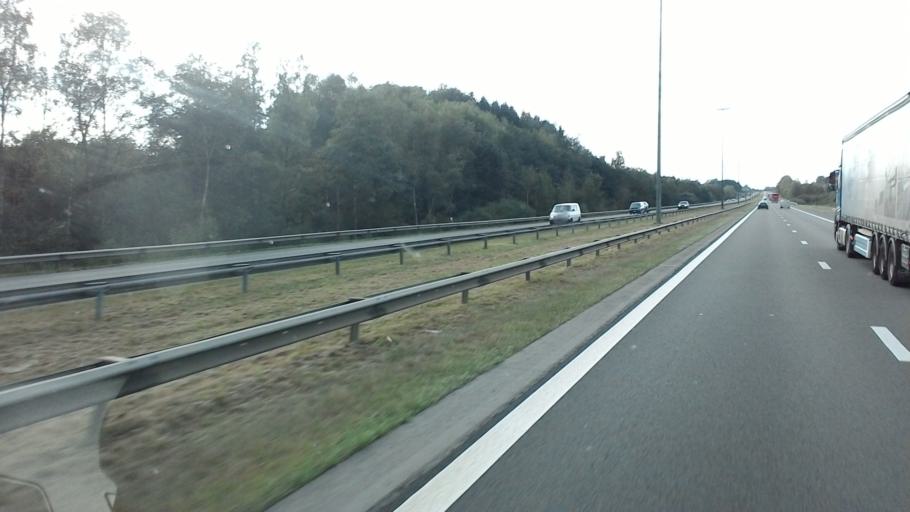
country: BE
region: Wallonia
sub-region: Province du Luxembourg
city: Attert
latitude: 49.6908
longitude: 5.7301
